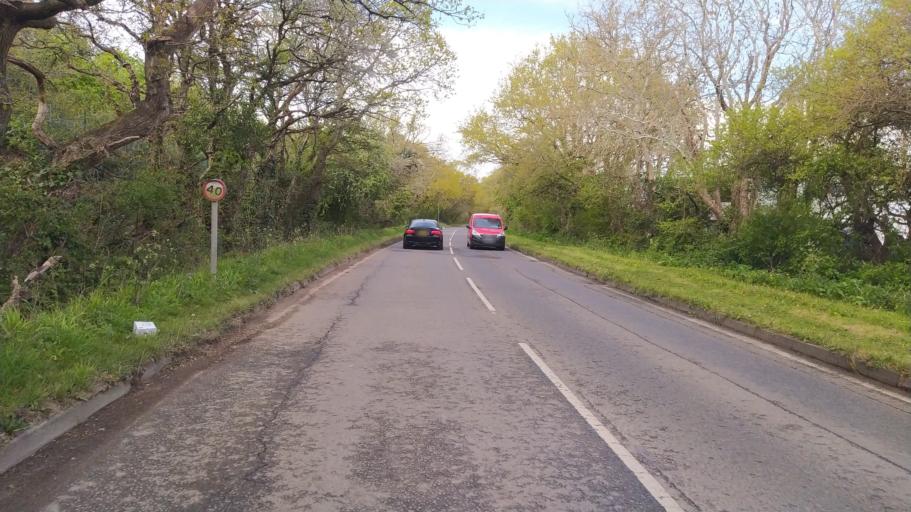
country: GB
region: England
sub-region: Hampshire
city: Netley
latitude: 50.8852
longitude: -1.3422
